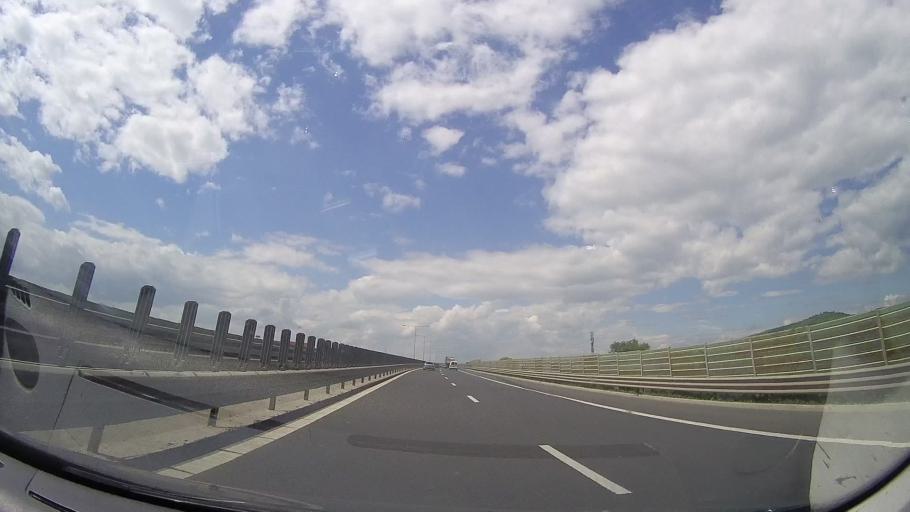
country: RO
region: Sibiu
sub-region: Municipiul Sibiu
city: Sibiu
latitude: 45.8069
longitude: 24.1763
